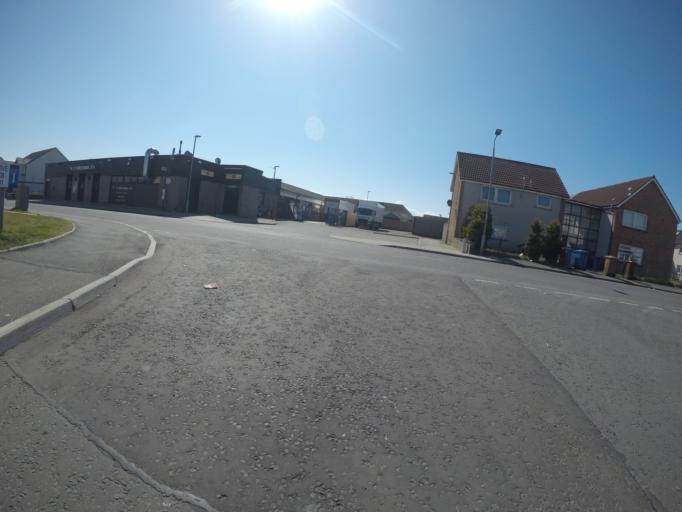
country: GB
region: Scotland
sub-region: North Ayrshire
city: Irvine
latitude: 55.6287
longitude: -4.6661
